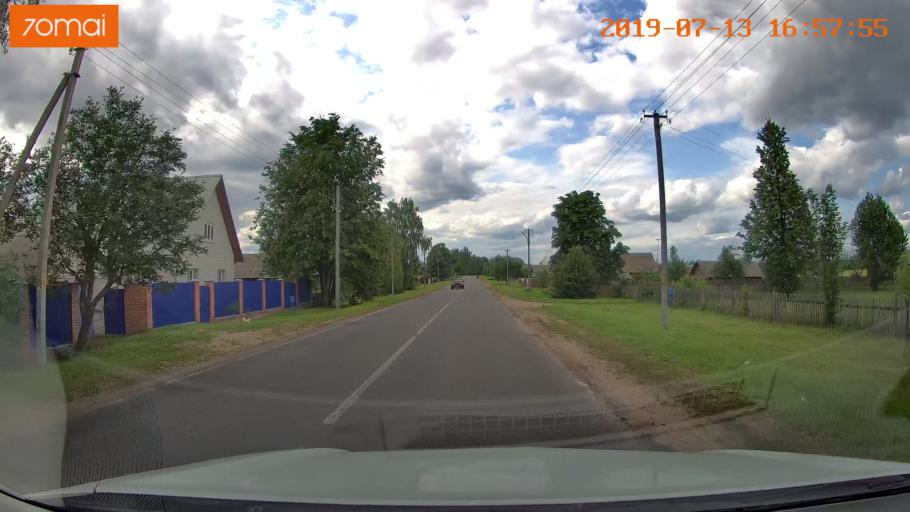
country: BY
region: Mogilev
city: Kirawsk
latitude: 53.2838
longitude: 29.4470
